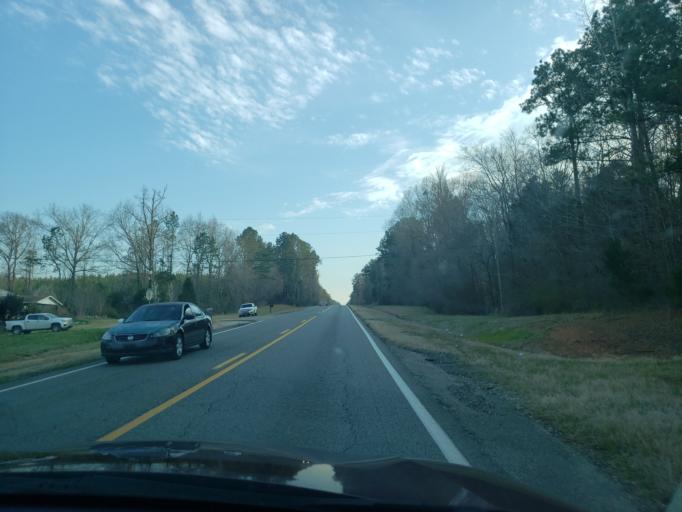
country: US
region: Alabama
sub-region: Hale County
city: Greensboro
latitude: 32.7581
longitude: -87.5853
